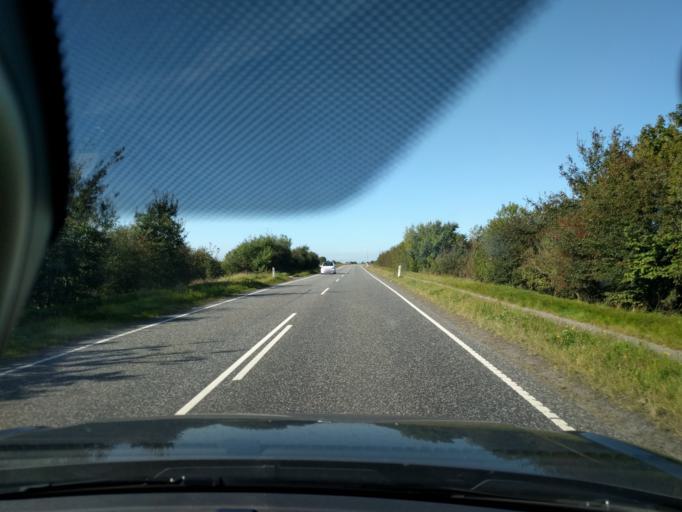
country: DK
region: North Denmark
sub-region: Vesthimmerland Kommune
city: Alestrup
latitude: 56.7116
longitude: 9.6205
